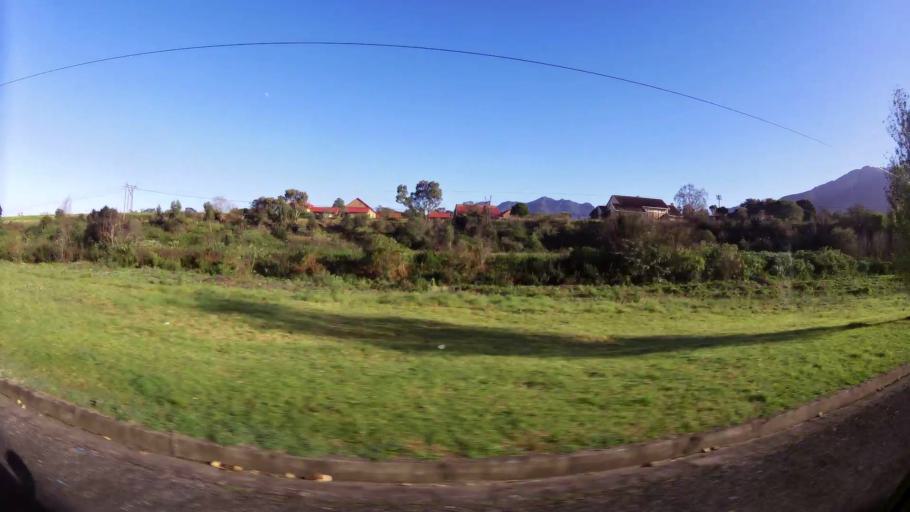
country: ZA
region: Western Cape
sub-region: Eden District Municipality
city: George
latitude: -33.9575
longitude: 22.4496
